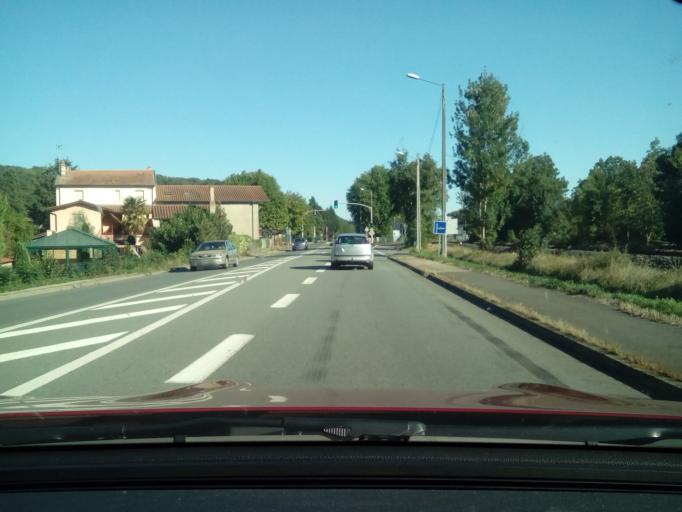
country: FR
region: Rhone-Alpes
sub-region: Departement du Rhone
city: Chessy
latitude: 45.8767
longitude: 4.6430
